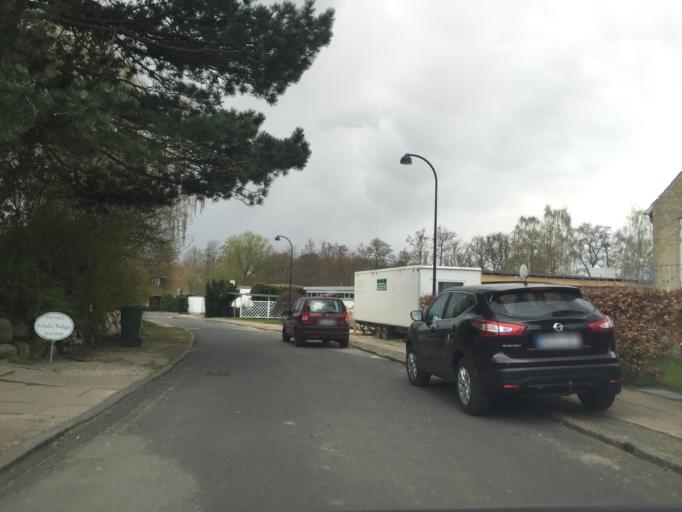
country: DK
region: Capital Region
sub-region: Gentofte Kommune
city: Charlottenlund
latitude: 55.7655
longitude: 12.5668
